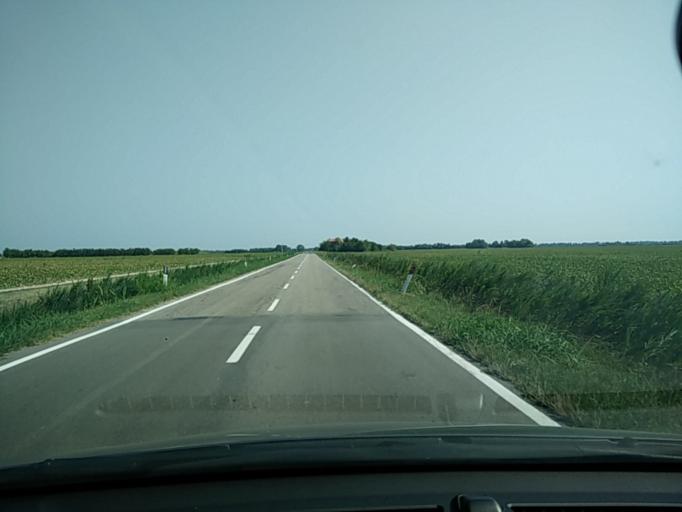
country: IT
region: Veneto
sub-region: Provincia di Venezia
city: La Salute di Livenza
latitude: 45.6399
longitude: 12.8280
